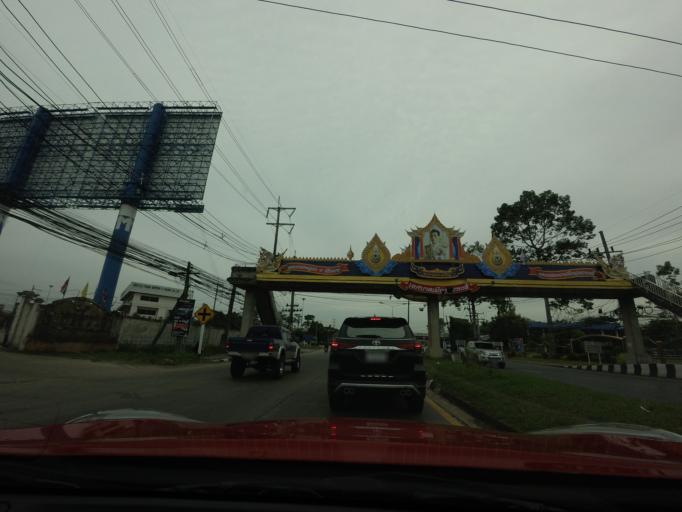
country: TH
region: Songkhla
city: Hat Yai
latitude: 6.9770
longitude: 100.4791
